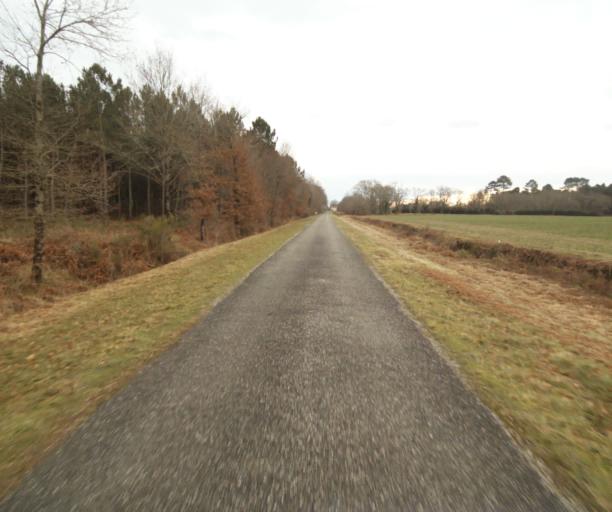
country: FR
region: Aquitaine
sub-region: Departement des Landes
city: Gabarret
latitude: 44.0174
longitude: -0.0391
